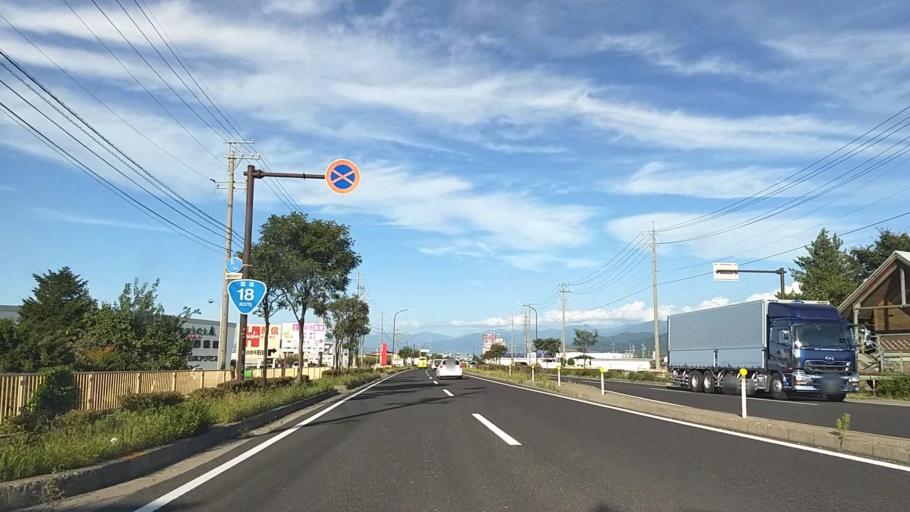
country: JP
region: Nagano
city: Nagano-shi
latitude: 36.5875
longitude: 138.1706
